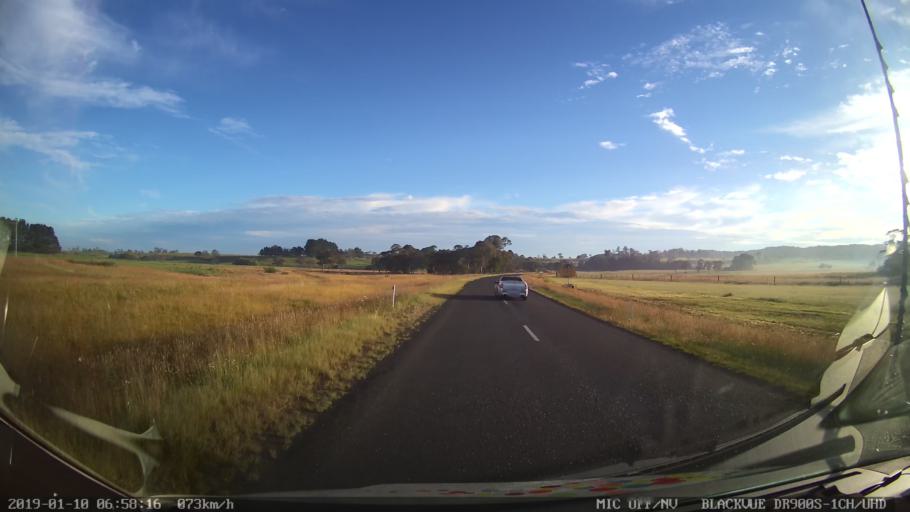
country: AU
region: New South Wales
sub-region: Bellingen
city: Dorrigo
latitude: -30.3849
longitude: 152.3610
